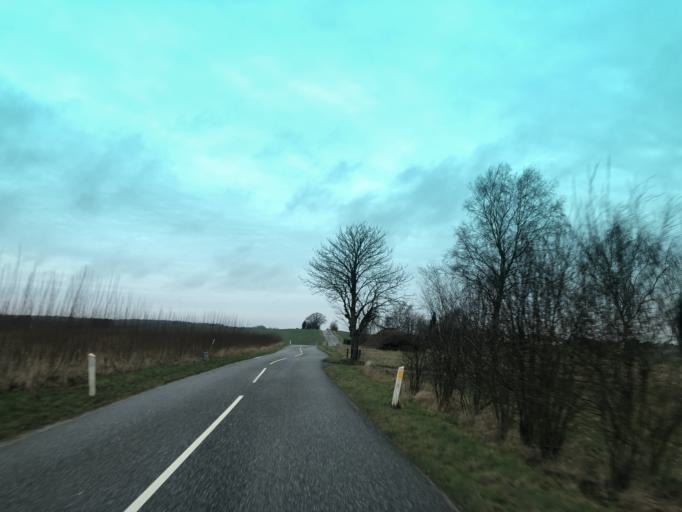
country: DK
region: Capital Region
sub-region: Allerod Kommune
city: Lynge
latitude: 55.8528
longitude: 12.2411
